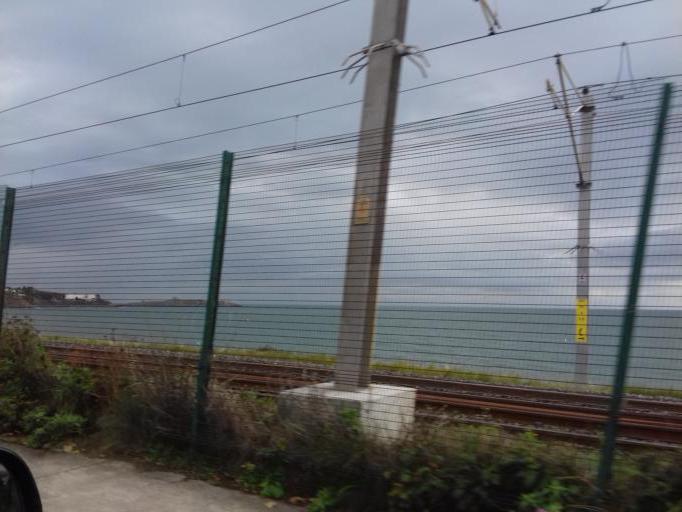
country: IE
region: Leinster
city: Dalkey
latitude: 53.2585
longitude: -6.1127
